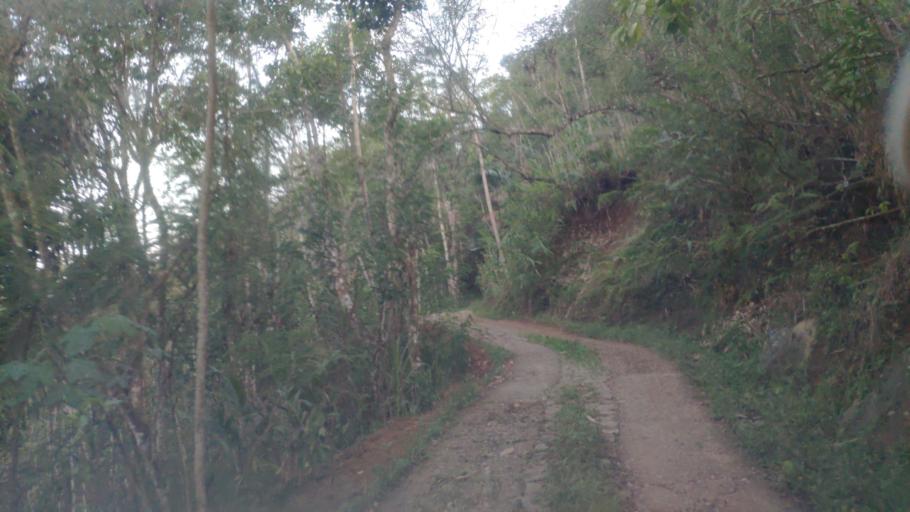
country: ID
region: Central Java
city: Buaran
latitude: -7.2603
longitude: 109.5715
